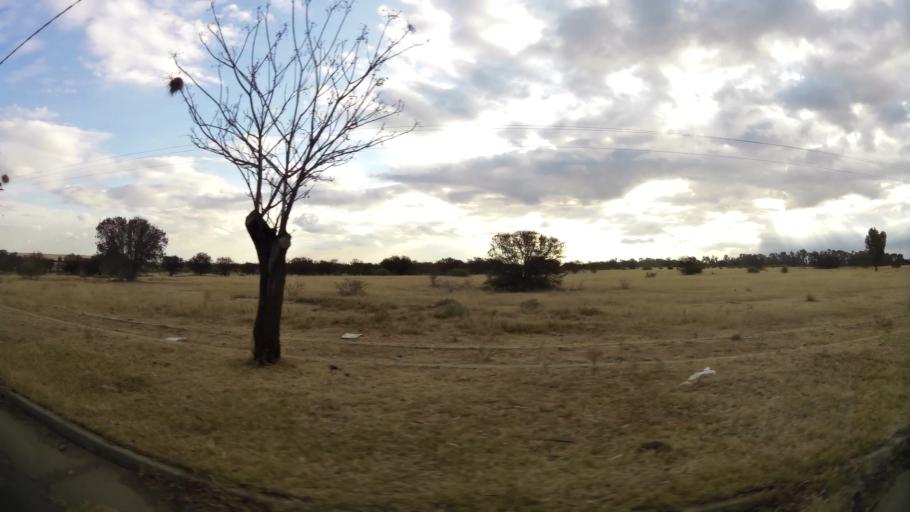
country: ZA
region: Orange Free State
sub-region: Lejweleputswa District Municipality
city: Welkom
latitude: -28.0052
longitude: 26.7100
